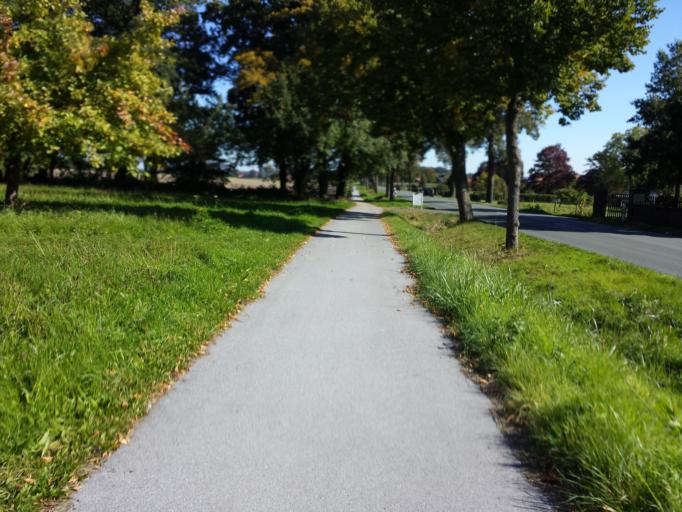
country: DE
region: North Rhine-Westphalia
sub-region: Regierungsbezirk Detmold
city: Langenberg
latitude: 51.7777
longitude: 8.3316
